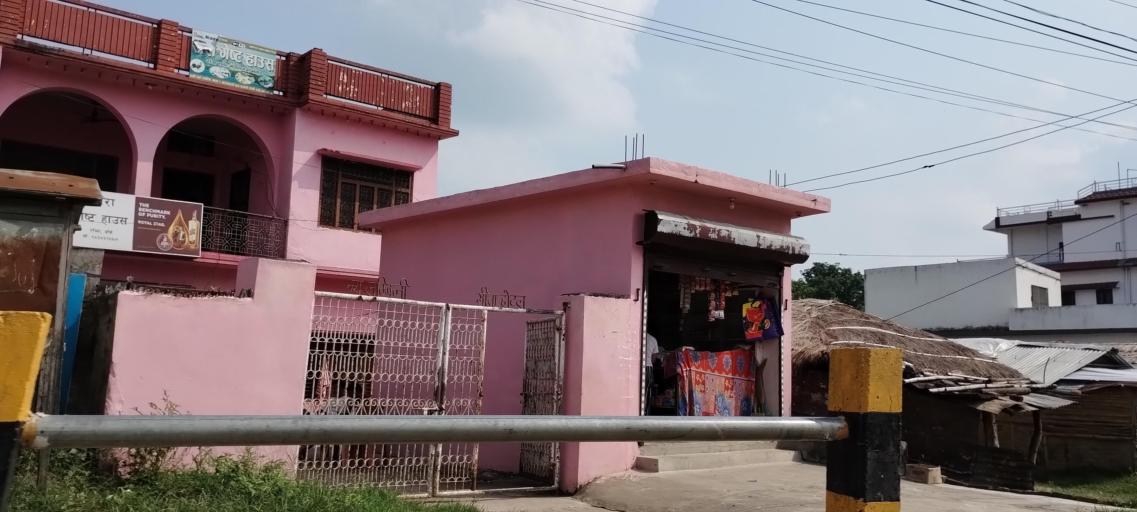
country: NP
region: Mid Western
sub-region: Bheri Zone
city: Nepalgunj
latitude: 28.0986
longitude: 81.6653
